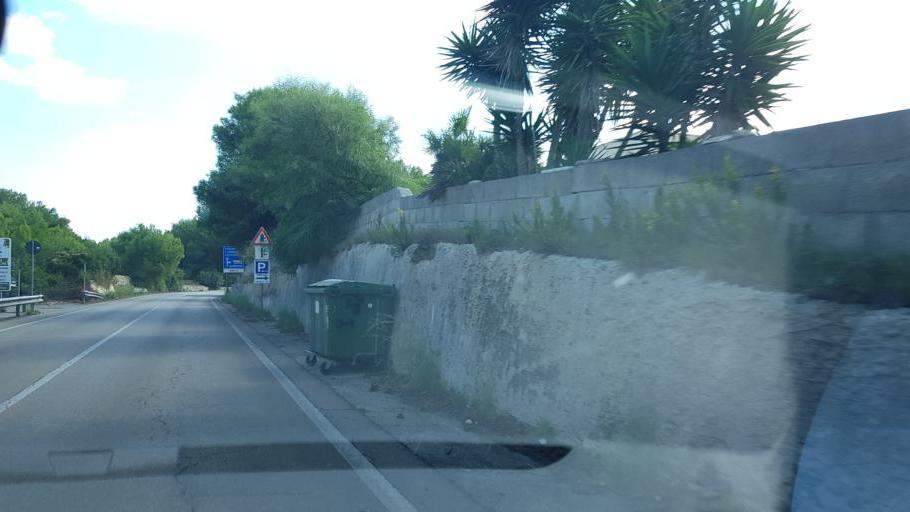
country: IT
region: Apulia
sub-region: Provincia di Lecce
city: Borgagne
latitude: 40.2689
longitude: 18.4307
